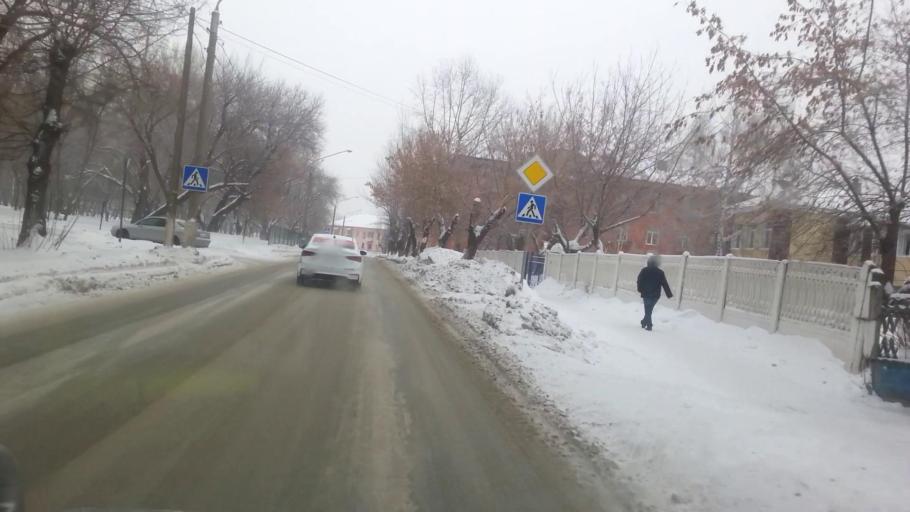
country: RU
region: Altai Krai
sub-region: Gorod Barnaulskiy
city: Barnaul
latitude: 53.3793
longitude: 83.7266
